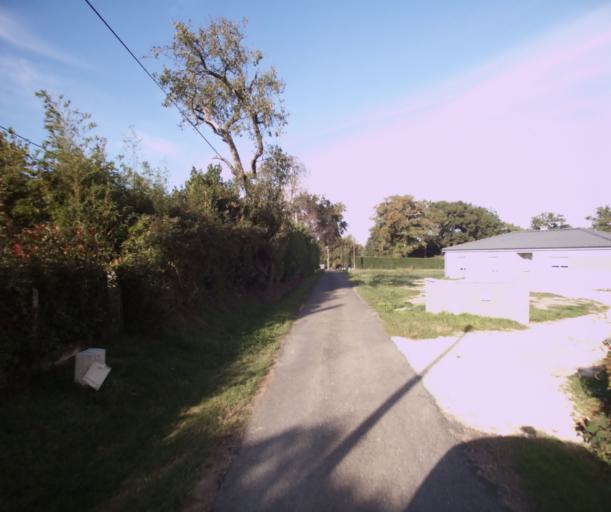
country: FR
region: Midi-Pyrenees
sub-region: Departement du Gers
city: Eauze
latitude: 43.8723
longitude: 0.0465
